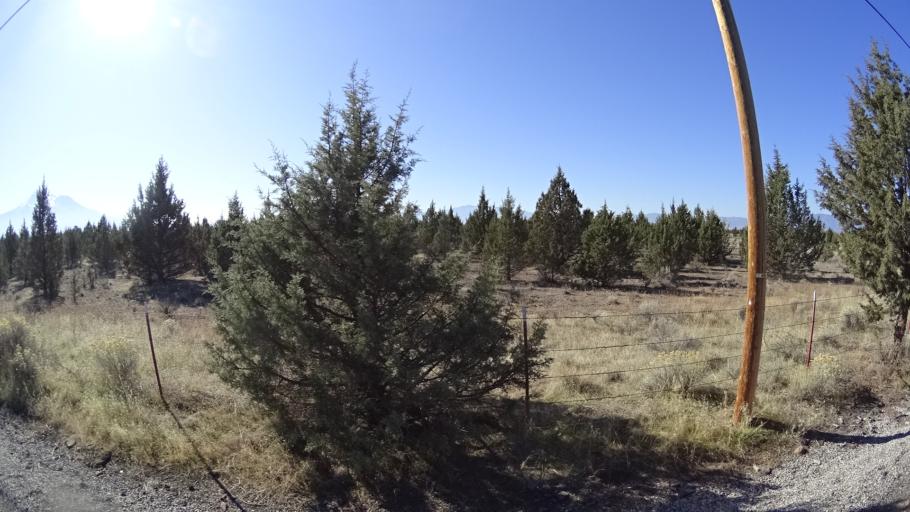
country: US
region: California
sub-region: Siskiyou County
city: Montague
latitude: 41.6449
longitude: -122.3545
